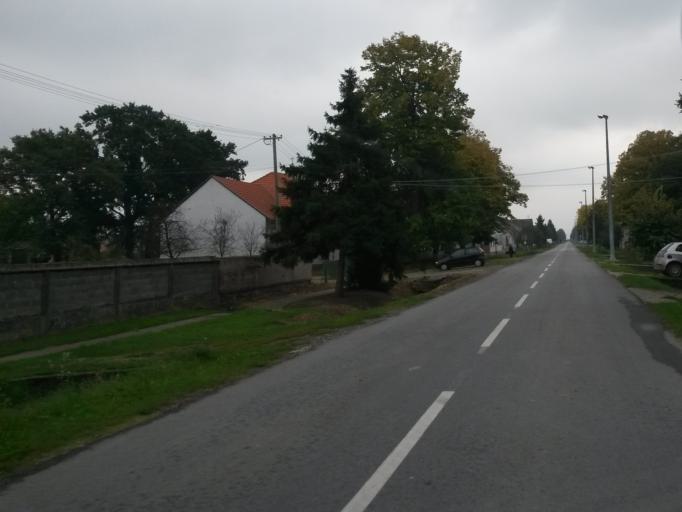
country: HR
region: Osjecko-Baranjska
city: Visnjevac
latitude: 45.5258
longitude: 18.6269
